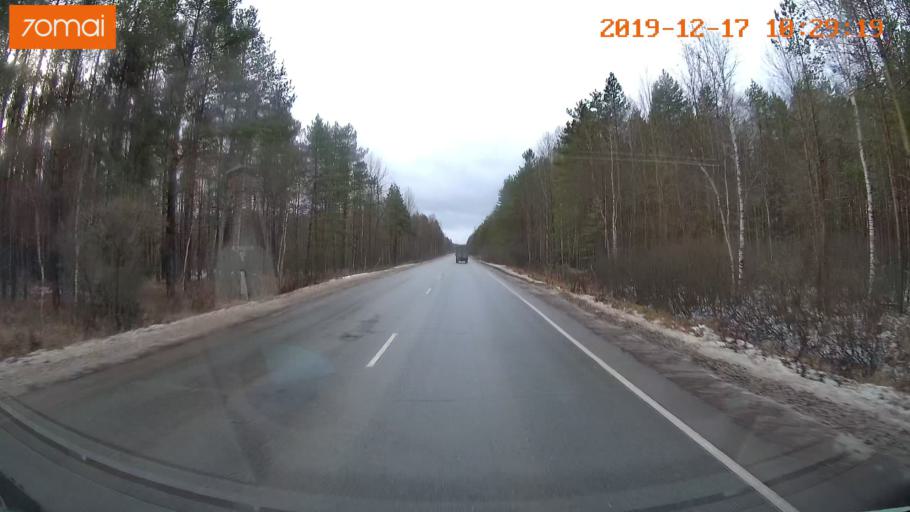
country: RU
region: Vladimir
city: Anopino
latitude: 55.6534
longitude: 40.7221
